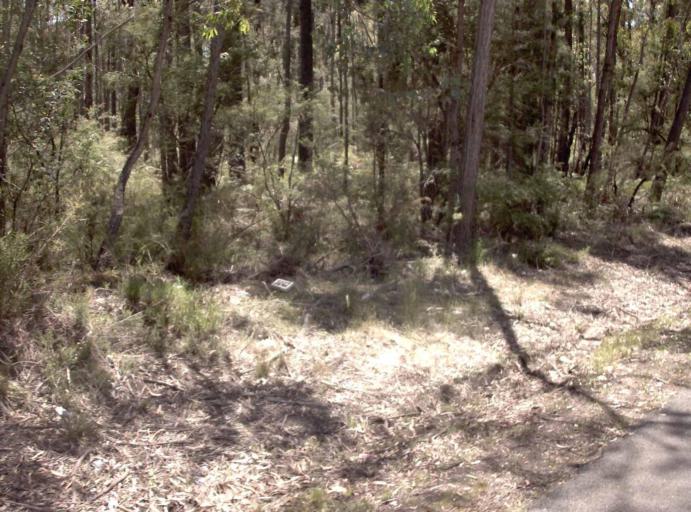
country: AU
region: Victoria
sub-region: East Gippsland
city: Lakes Entrance
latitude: -37.7540
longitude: 148.0672
